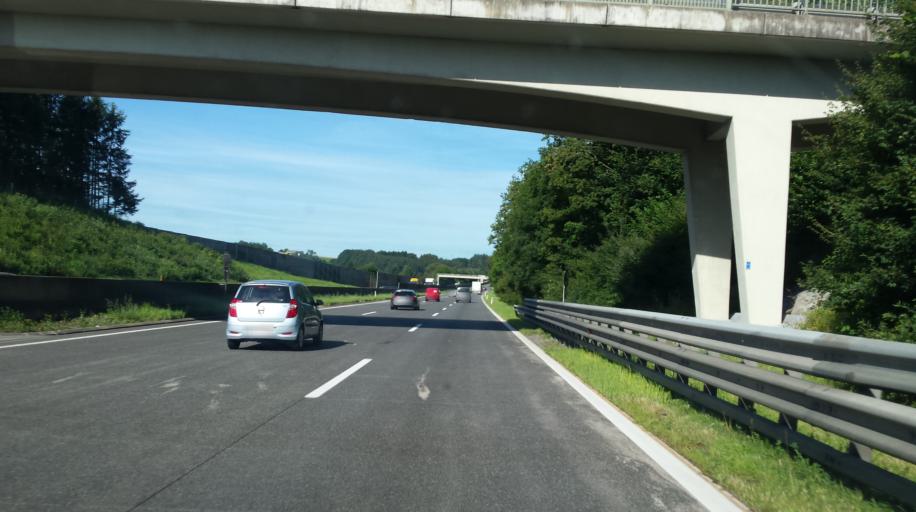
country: AT
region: Upper Austria
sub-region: Politischer Bezirk Vocklabruck
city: Seewalchen
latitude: 47.9566
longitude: 13.5525
